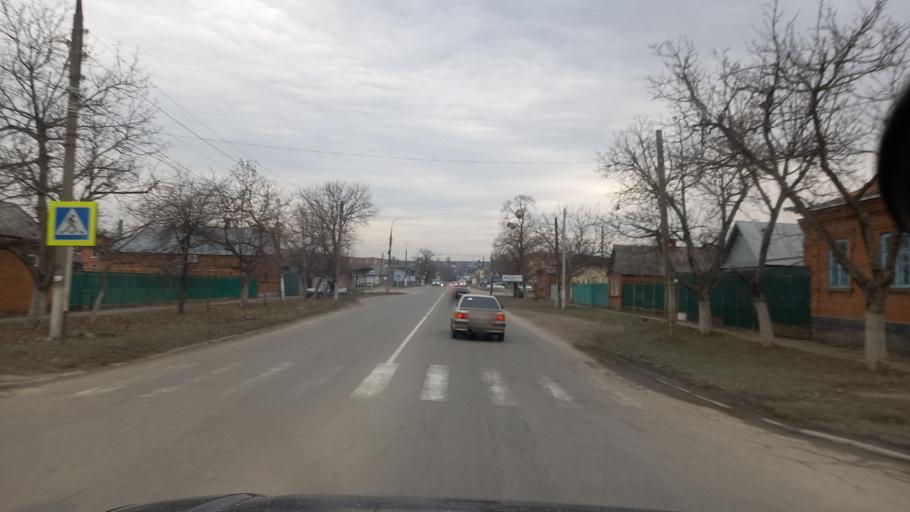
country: RU
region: Adygeya
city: Maykop
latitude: 44.5983
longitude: 40.1307
